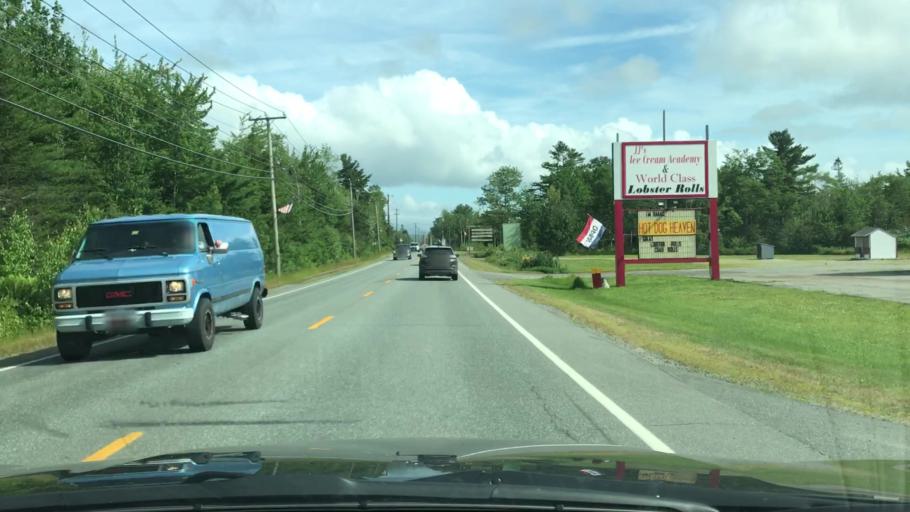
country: US
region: Maine
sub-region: Hancock County
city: Ellsworth
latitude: 44.5041
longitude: -68.3858
